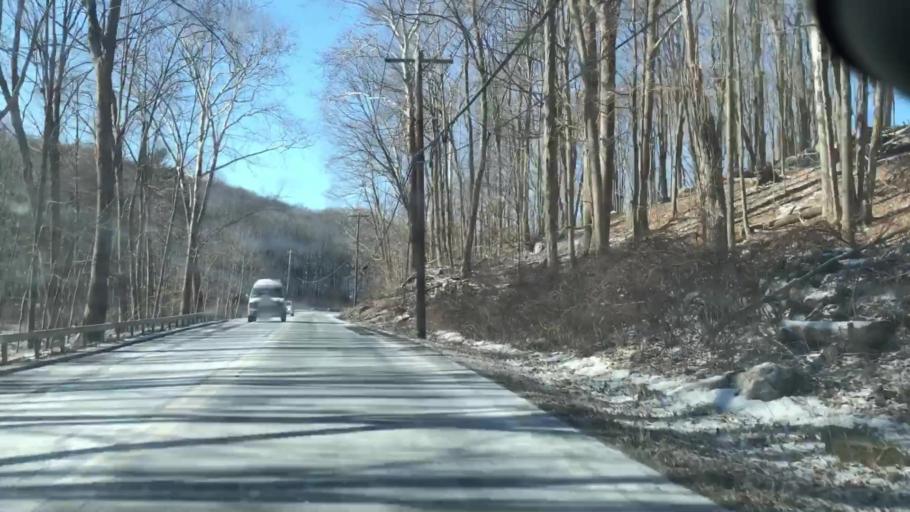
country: US
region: New York
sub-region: Putnam County
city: Carmel Hamlet
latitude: 41.3886
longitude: -73.6810
